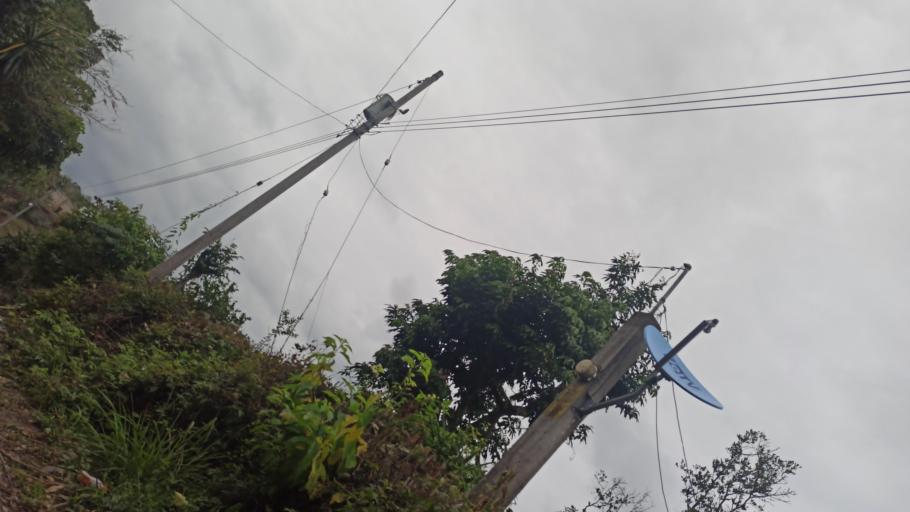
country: MX
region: Puebla
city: Espinal
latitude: 20.2893
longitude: -97.3936
